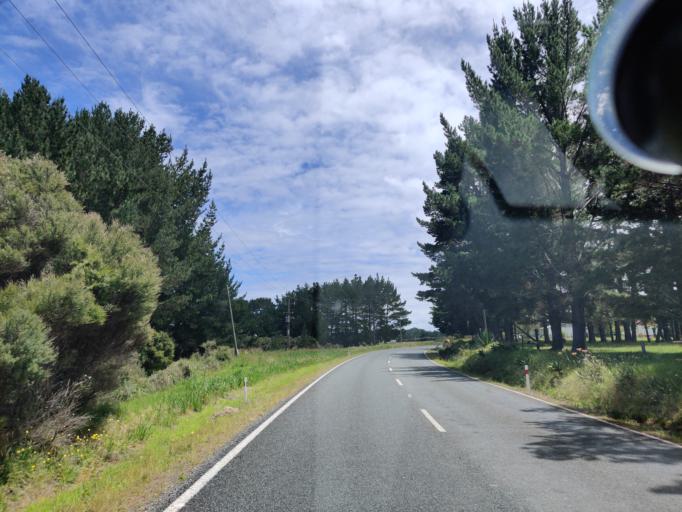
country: NZ
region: Northland
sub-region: Far North District
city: Kaitaia
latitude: -34.6678
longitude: 172.9760
